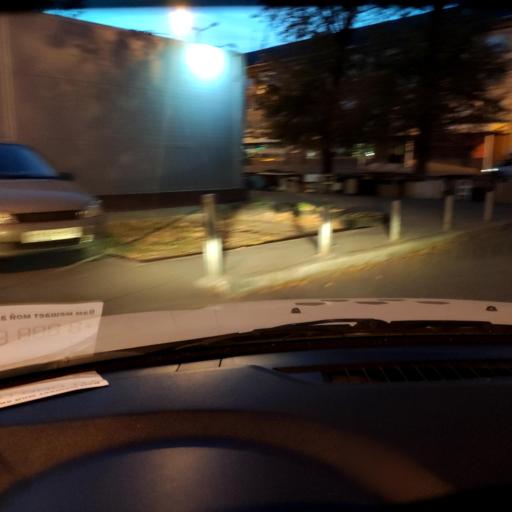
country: RU
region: Samara
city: Tol'yatti
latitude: 53.5070
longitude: 49.4021
